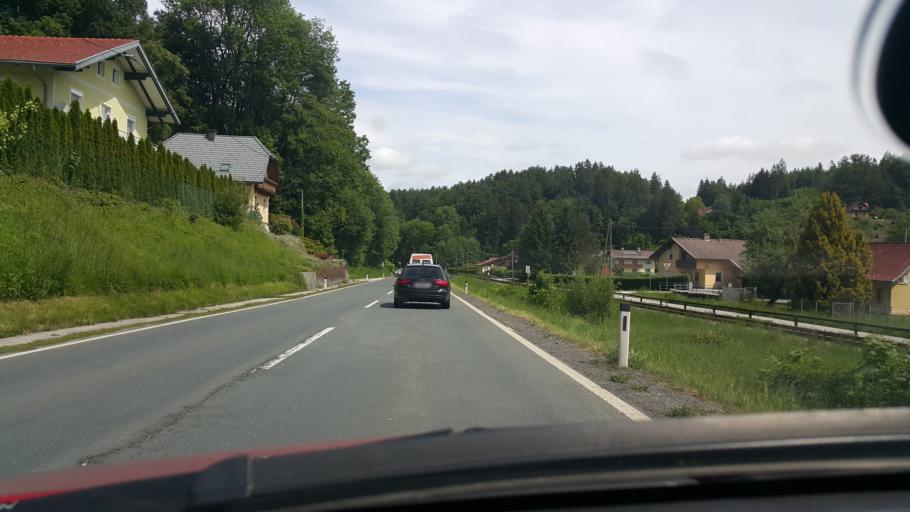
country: AT
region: Carinthia
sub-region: Politischer Bezirk Klagenfurt Land
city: Maria Rain
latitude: 46.5722
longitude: 14.2858
